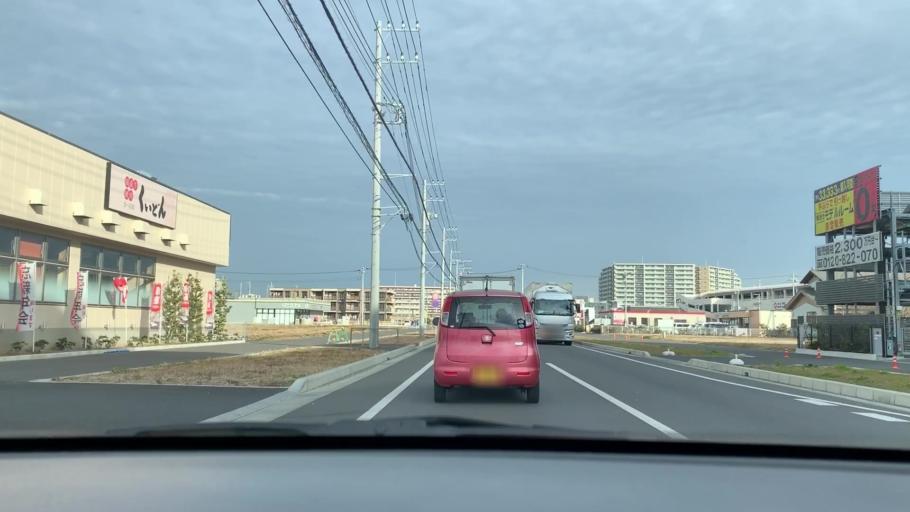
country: JP
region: Chiba
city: Nagareyama
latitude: 35.8299
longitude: 139.8958
